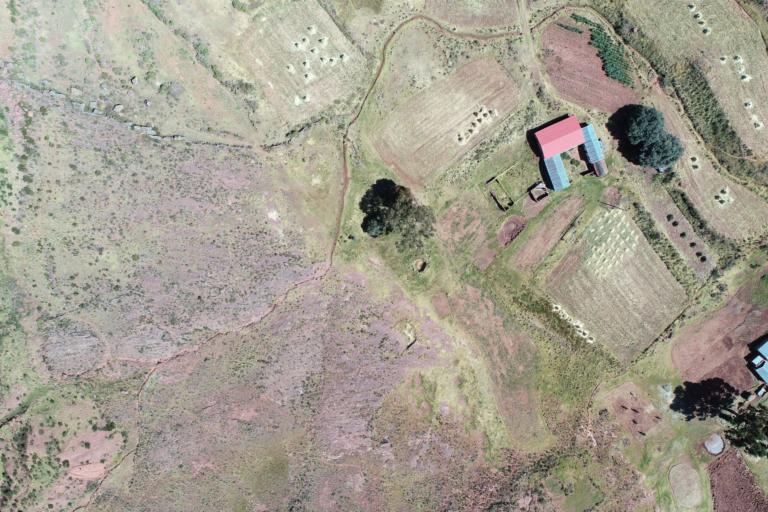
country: BO
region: La Paz
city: Tiahuanaco
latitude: -16.6052
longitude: -68.7801
